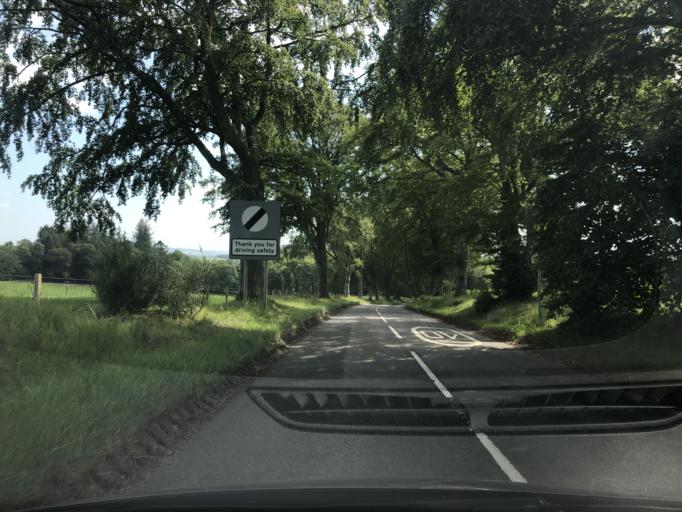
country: GB
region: Scotland
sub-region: Angus
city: Kirriemuir
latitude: 56.7277
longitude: -3.0029
